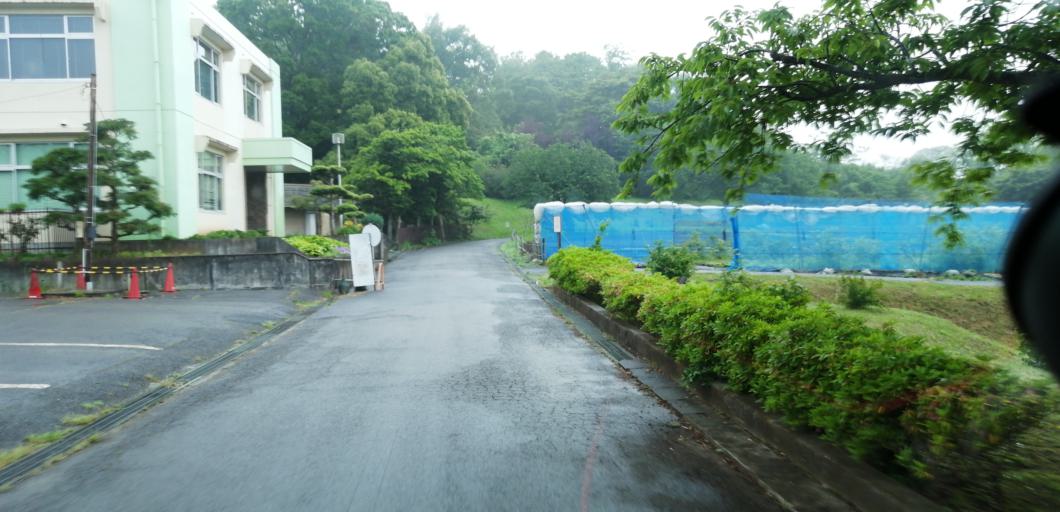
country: JP
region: Chiba
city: Ichihara
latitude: 35.4622
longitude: 140.1119
